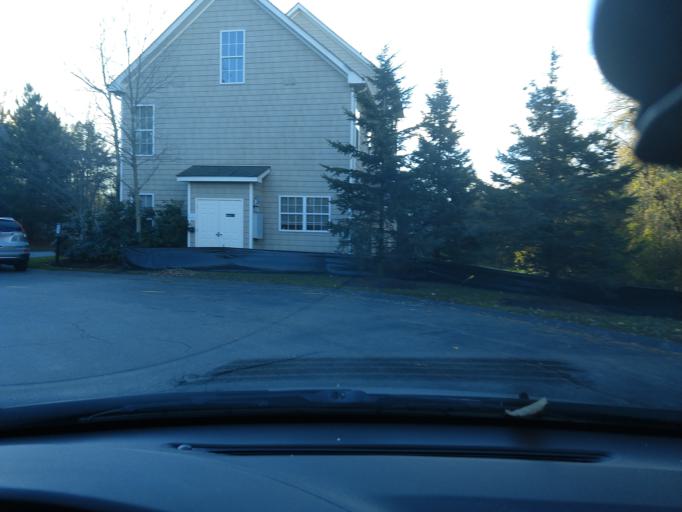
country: US
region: Massachusetts
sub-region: Middlesex County
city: Bedford
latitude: 42.4949
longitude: -71.2898
